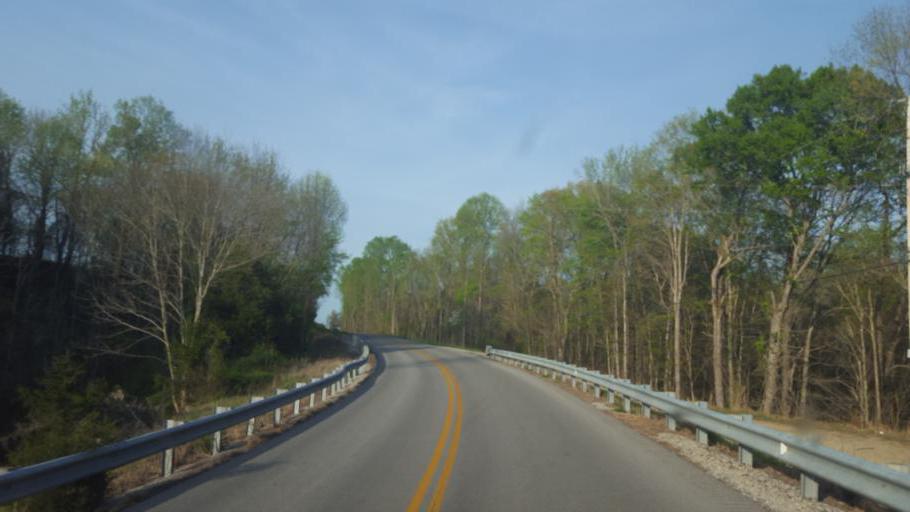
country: US
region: Kentucky
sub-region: Barren County
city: Glasgow
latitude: 36.9425
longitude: -86.0262
